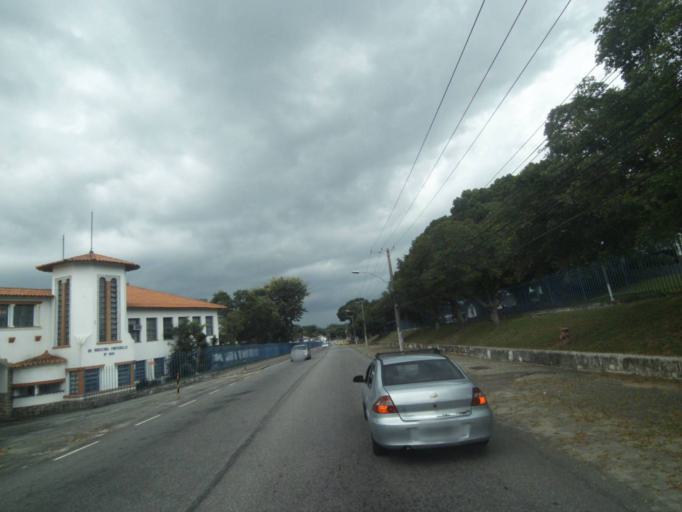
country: BR
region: Rio de Janeiro
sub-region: Sao Joao De Meriti
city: Sao Joao de Meriti
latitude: -22.8814
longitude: -43.3821
